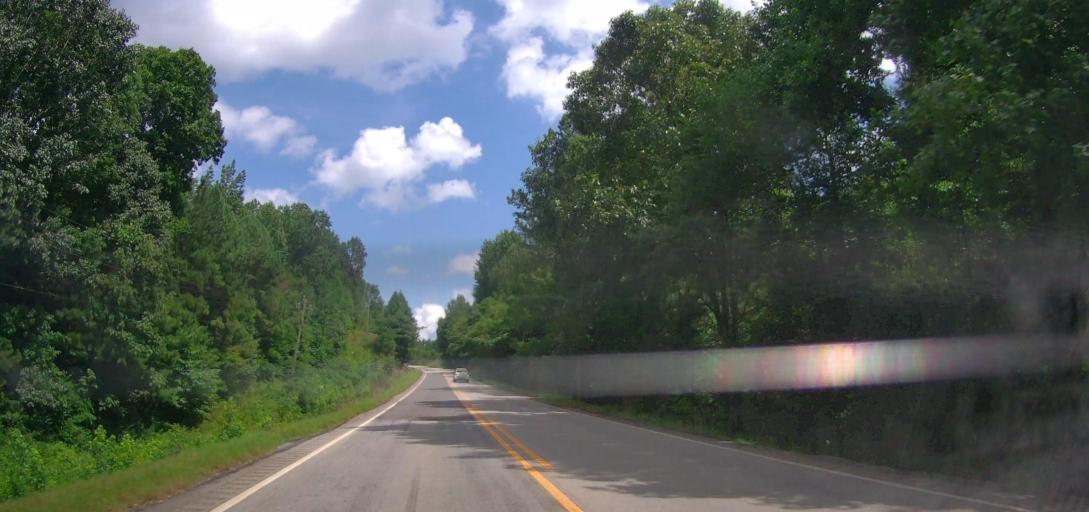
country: US
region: Georgia
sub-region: Carroll County
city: Bowdon
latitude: 33.5436
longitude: -85.3956
